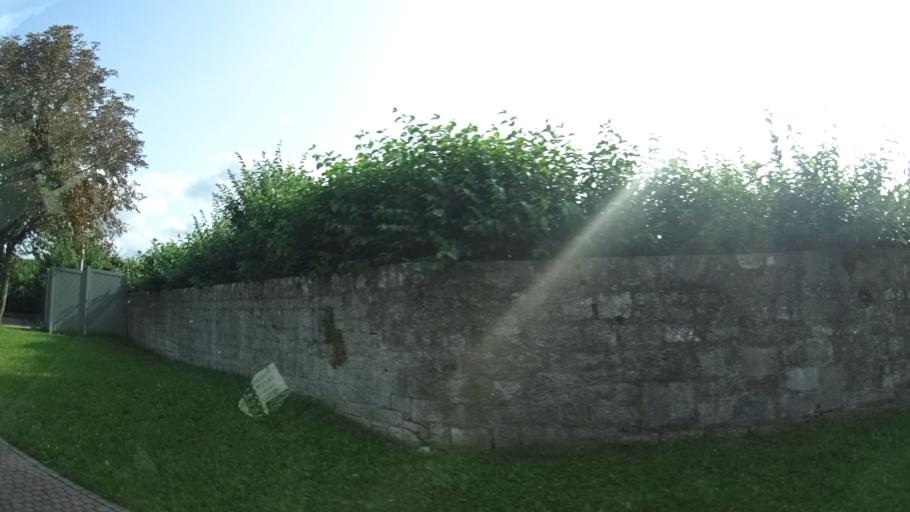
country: DE
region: Bavaria
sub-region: Regierungsbezirk Unterfranken
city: Zellingen
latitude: 49.8640
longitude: 9.8028
